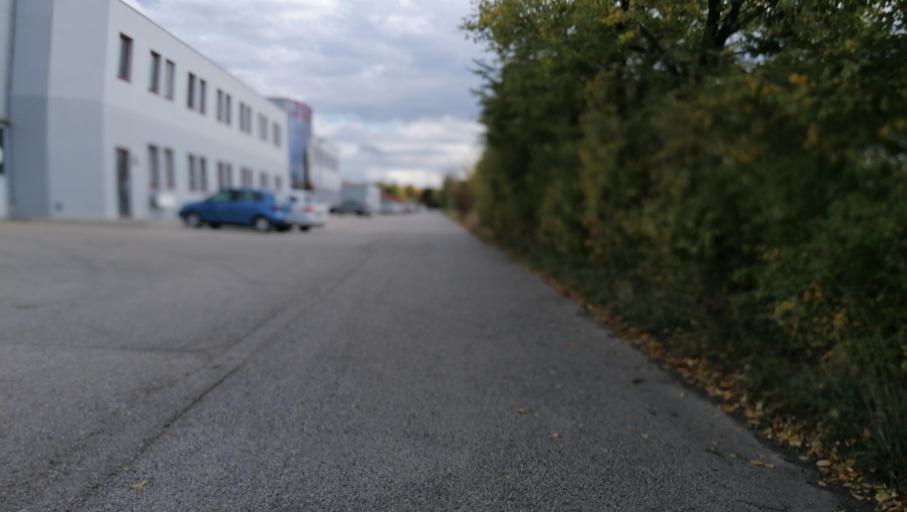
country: AT
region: Lower Austria
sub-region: Politischer Bezirk Baden
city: Tattendorf
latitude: 47.9488
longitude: 16.3115
